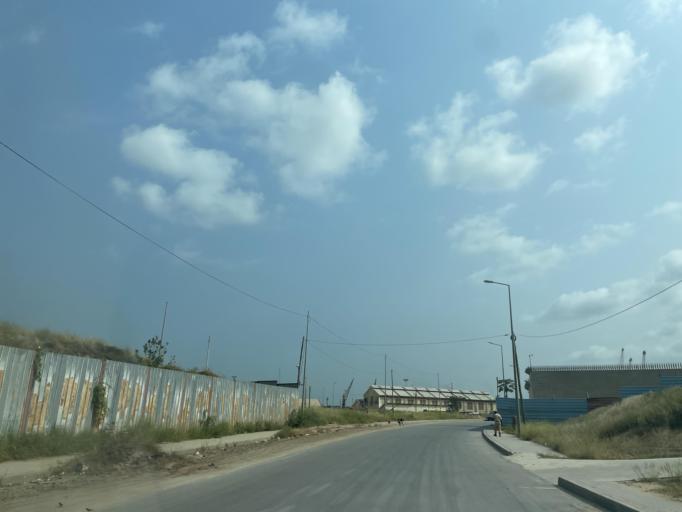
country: AO
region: Luanda
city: Luanda
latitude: -8.8052
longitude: 13.2467
